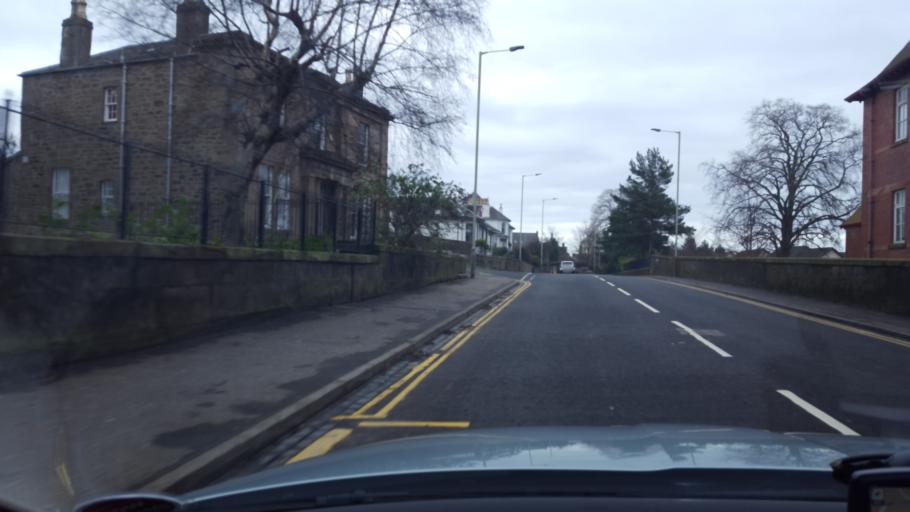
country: GB
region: Scotland
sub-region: Dundee City
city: Dundee
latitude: 56.4664
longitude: -2.9817
